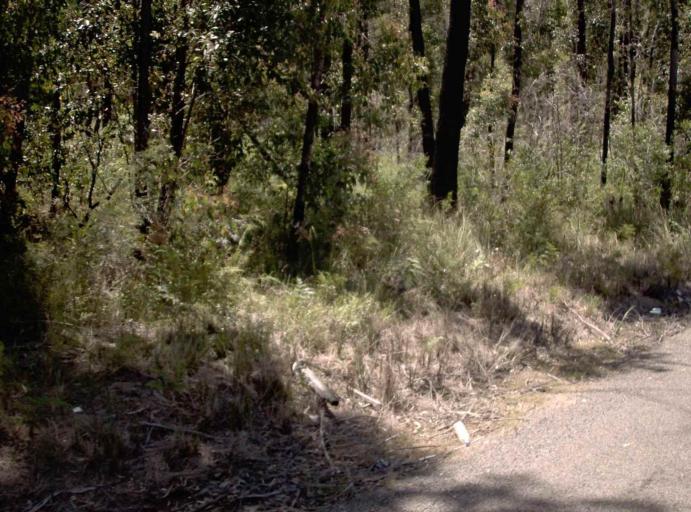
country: AU
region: Victoria
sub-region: East Gippsland
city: Lakes Entrance
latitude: -37.7515
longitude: 148.2170
